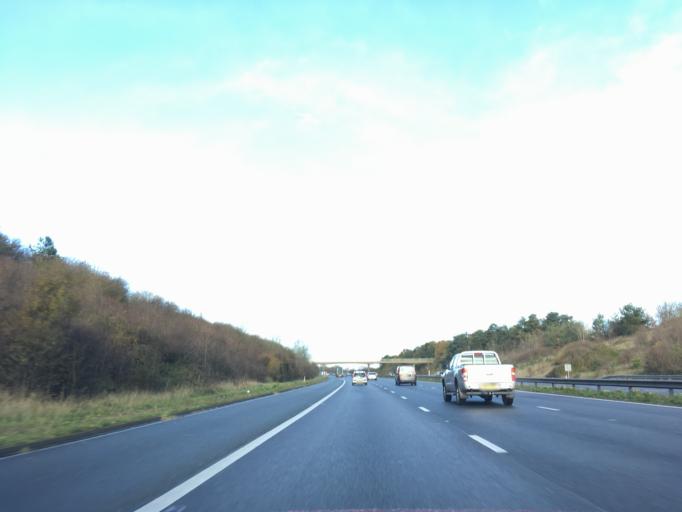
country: GB
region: England
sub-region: Worcestershire
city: Bredon
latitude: 52.0182
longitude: -2.1204
